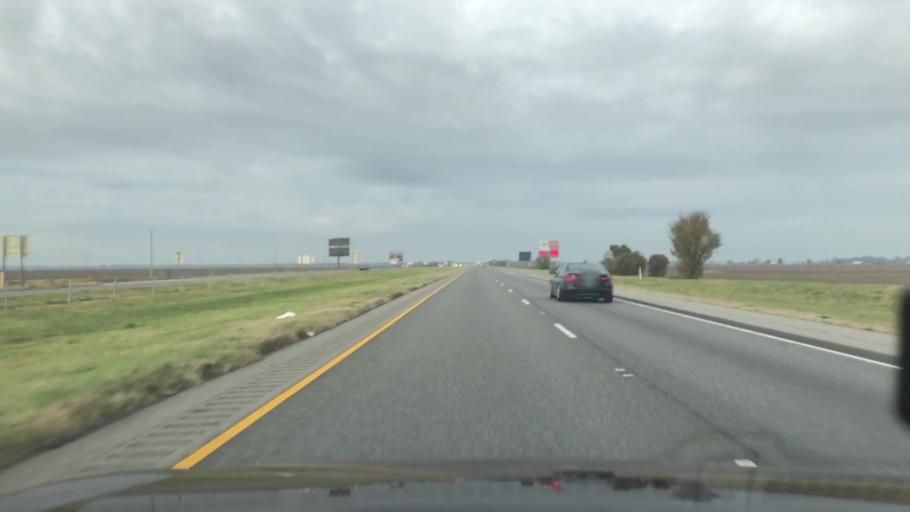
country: US
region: Mississippi
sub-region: Warren County
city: Vicksburg
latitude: 32.3210
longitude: -90.9644
